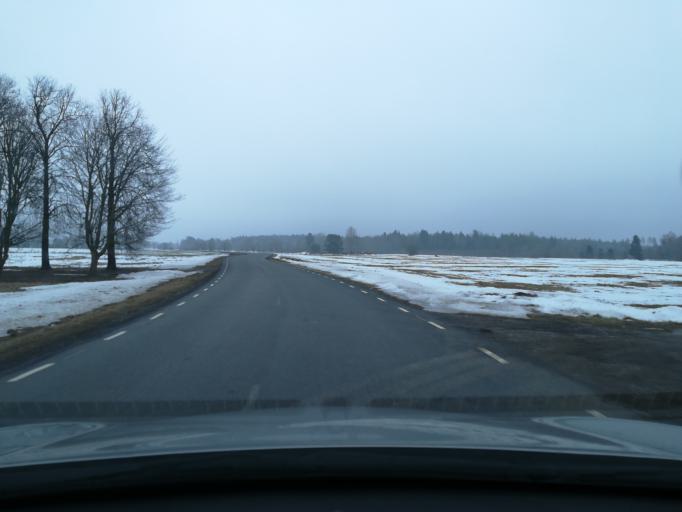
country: EE
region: Harju
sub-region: Kuusalu vald
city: Kuusalu
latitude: 59.4705
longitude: 25.5692
